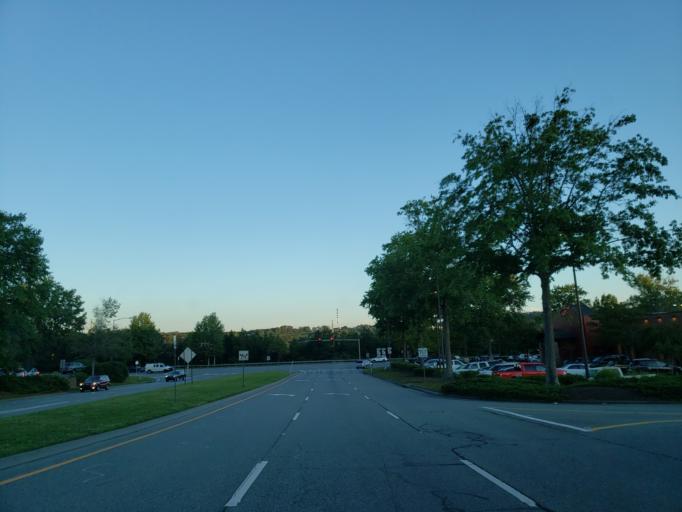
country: US
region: Georgia
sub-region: Cherokee County
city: Canton
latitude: 34.2498
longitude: -84.4782
